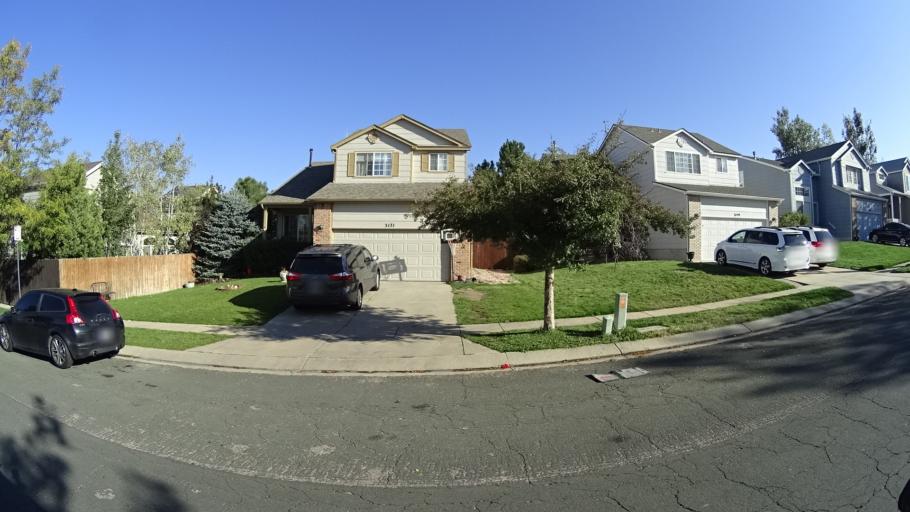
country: US
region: Colorado
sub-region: El Paso County
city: Cimarron Hills
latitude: 38.8789
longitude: -104.6979
